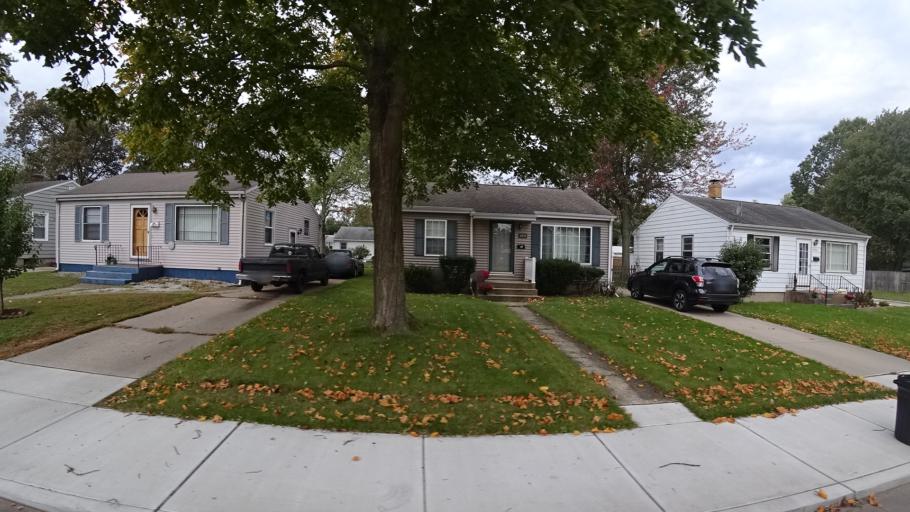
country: US
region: Indiana
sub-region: LaPorte County
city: Michigan City
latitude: 41.6975
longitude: -86.8811
